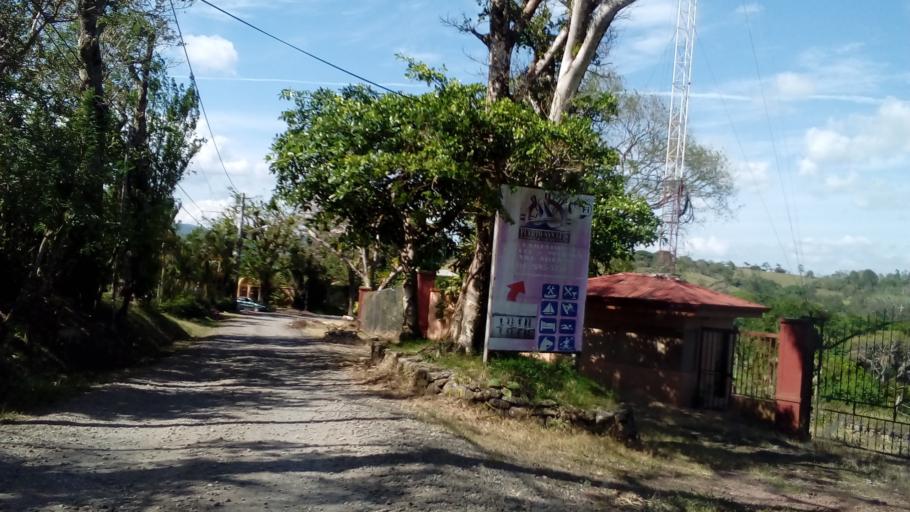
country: CR
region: Guanacaste
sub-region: Canton de Tilaran
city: Tilaran
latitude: 10.5068
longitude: -84.9373
